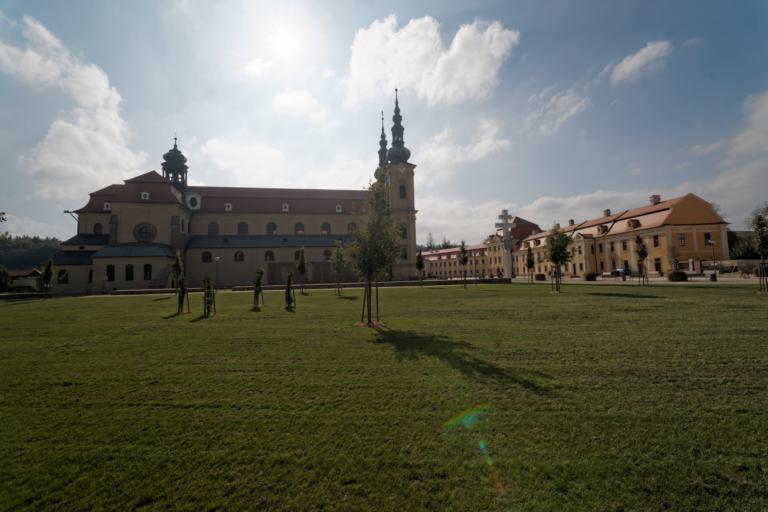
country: CZ
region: Zlin
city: Velehrad
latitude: 49.1044
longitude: 17.3958
